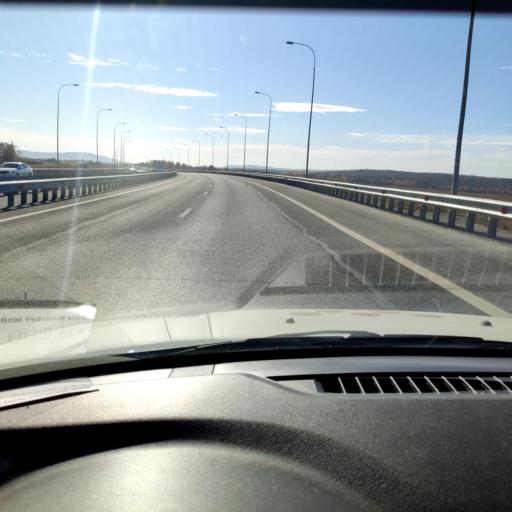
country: RU
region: Samara
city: Bereza
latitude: 53.4996
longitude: 50.1164
